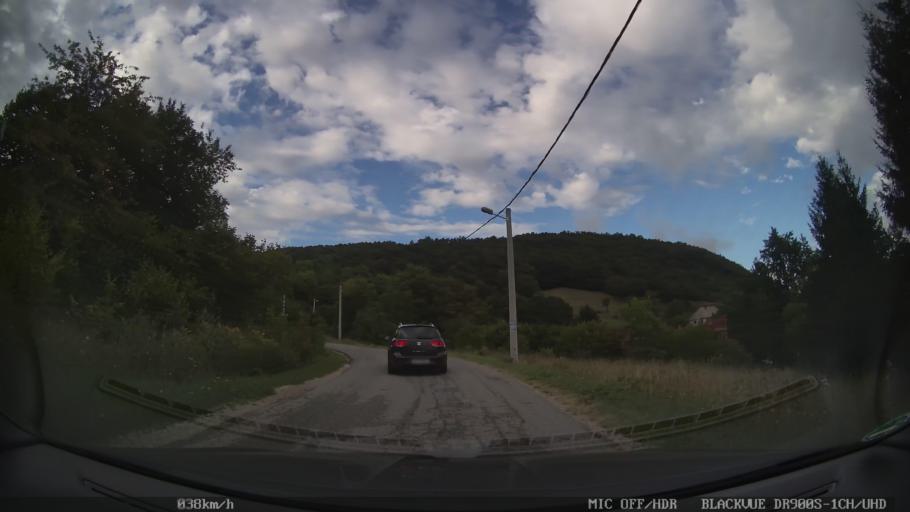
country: HR
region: Licko-Senjska
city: Jezerce
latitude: 44.9236
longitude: 15.6006
